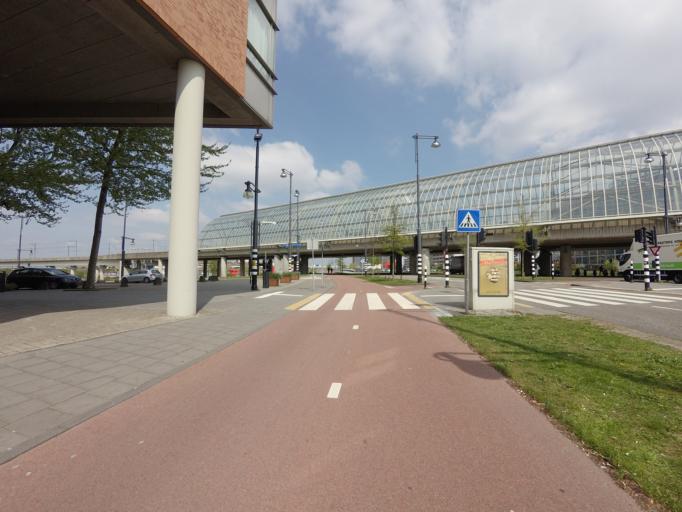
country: NL
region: North Holland
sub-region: Gemeente Zaanstad
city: Zaandam
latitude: 52.3873
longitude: 4.8358
